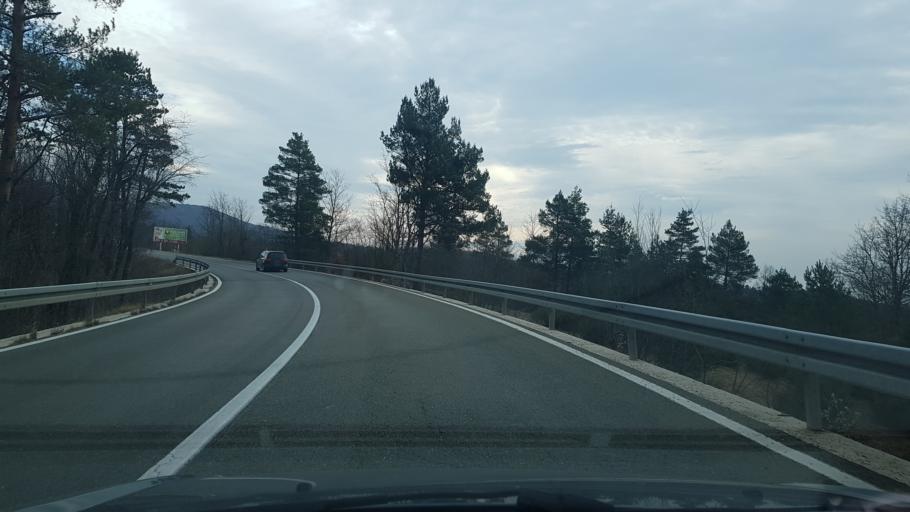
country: SI
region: Ilirska Bistrica
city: Ilirska Bistrica
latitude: 45.4765
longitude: 14.2668
